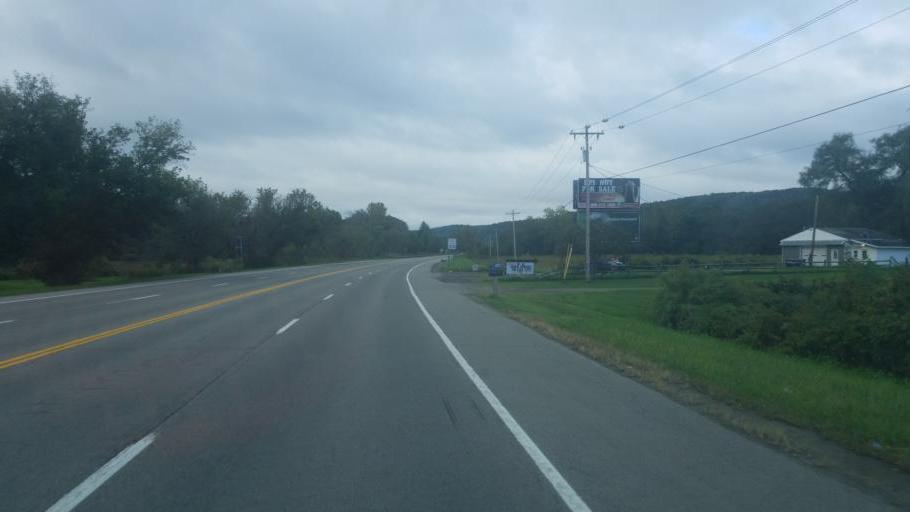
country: US
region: New York
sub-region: Cattaraugus County
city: Weston Mills
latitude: 42.1726
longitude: -78.3847
